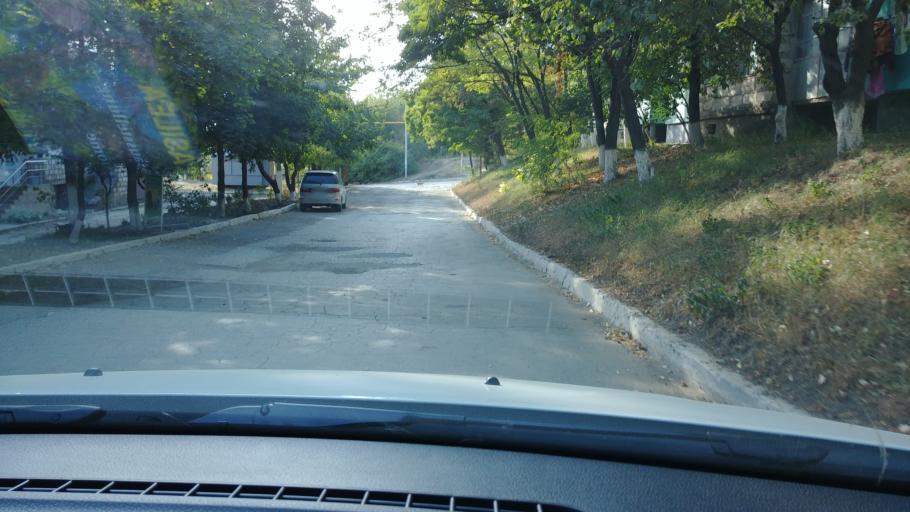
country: MD
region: Rezina
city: Rezina
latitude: 47.7460
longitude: 28.9573
